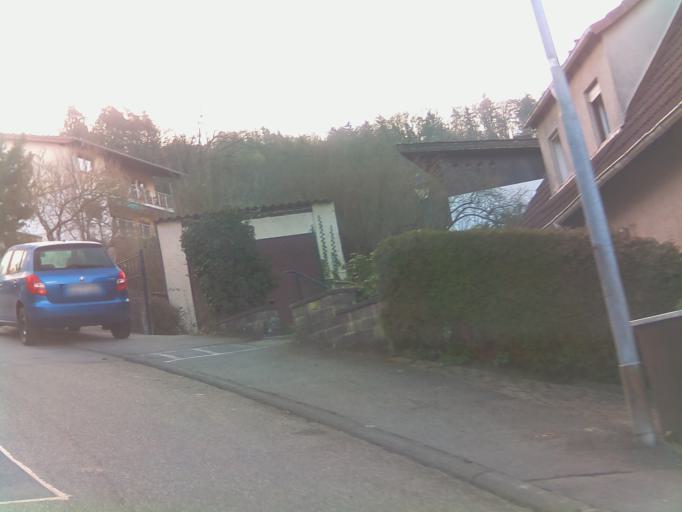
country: DE
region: Baden-Wuerttemberg
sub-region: Karlsruhe Region
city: Mosbach
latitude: 49.3495
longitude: 9.1533
